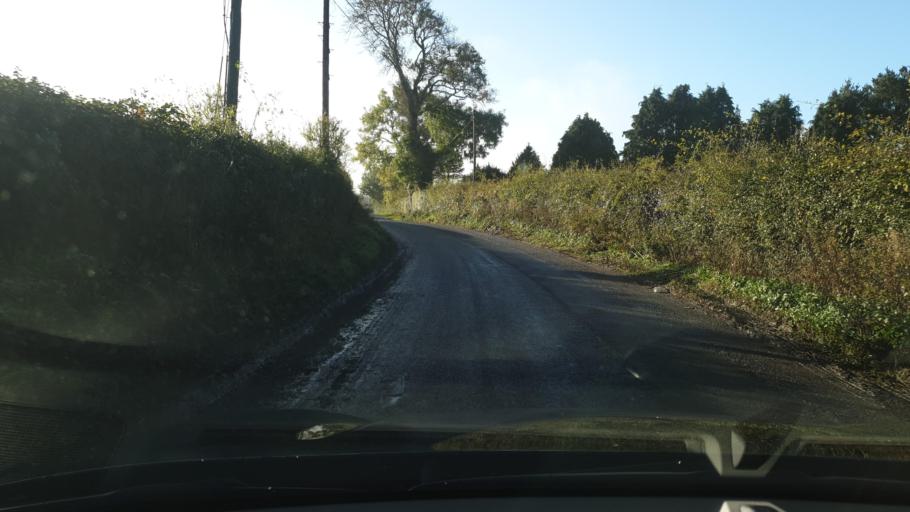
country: IE
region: Leinster
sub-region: An Mhi
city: Ashbourne
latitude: 53.4764
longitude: -6.3750
